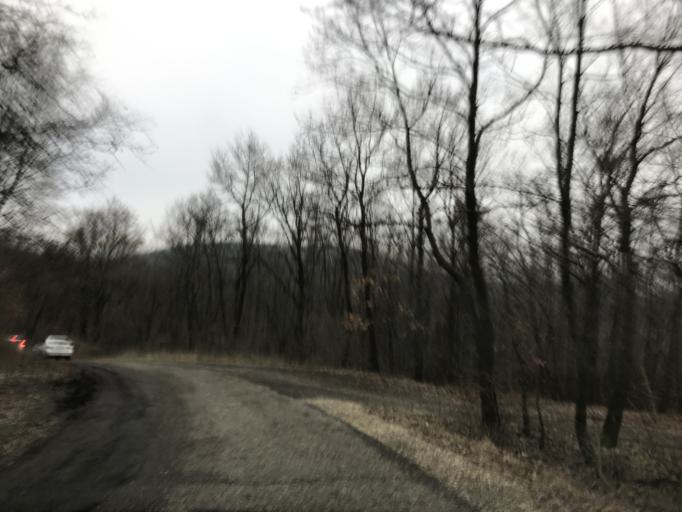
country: HU
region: Pest
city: Nagykovacsi
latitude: 47.6892
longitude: 18.9954
